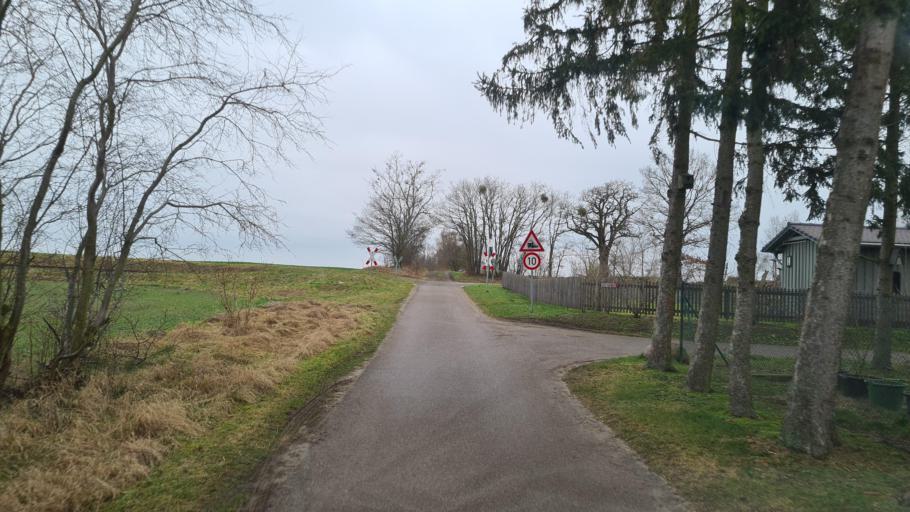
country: DE
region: Brandenburg
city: Zehdenick
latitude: 52.9355
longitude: 13.2598
